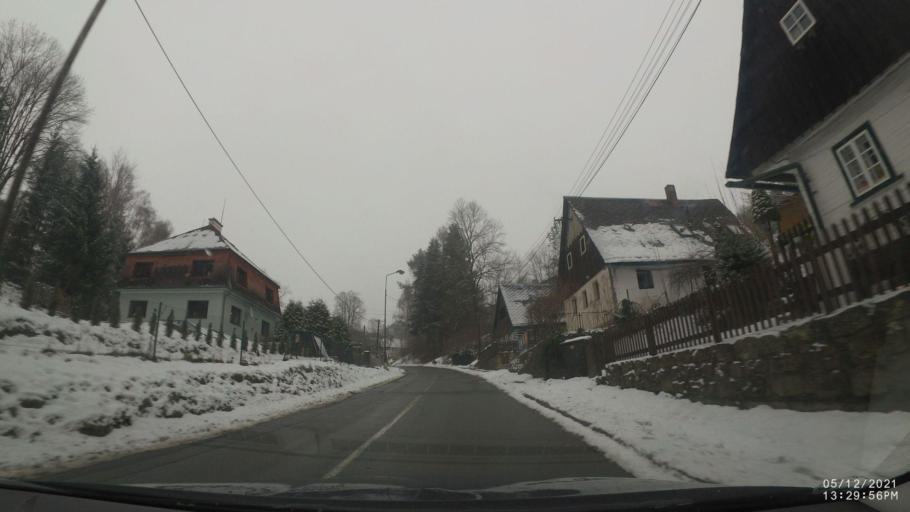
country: CZ
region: Kralovehradecky
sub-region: Okres Nachod
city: Police nad Metuji
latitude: 50.5092
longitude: 16.2205
